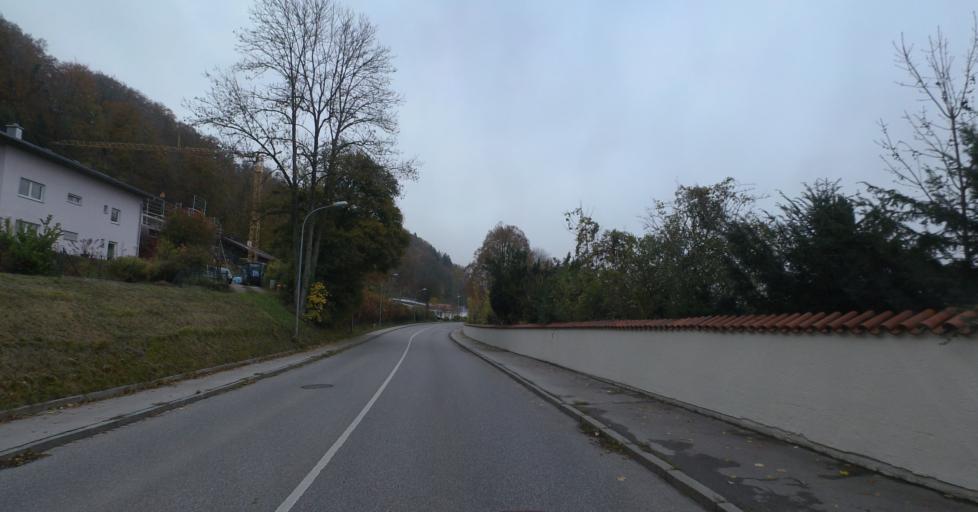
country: DE
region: Bavaria
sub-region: Upper Bavaria
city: Trostberg an der Alz
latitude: 48.0323
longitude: 12.5575
